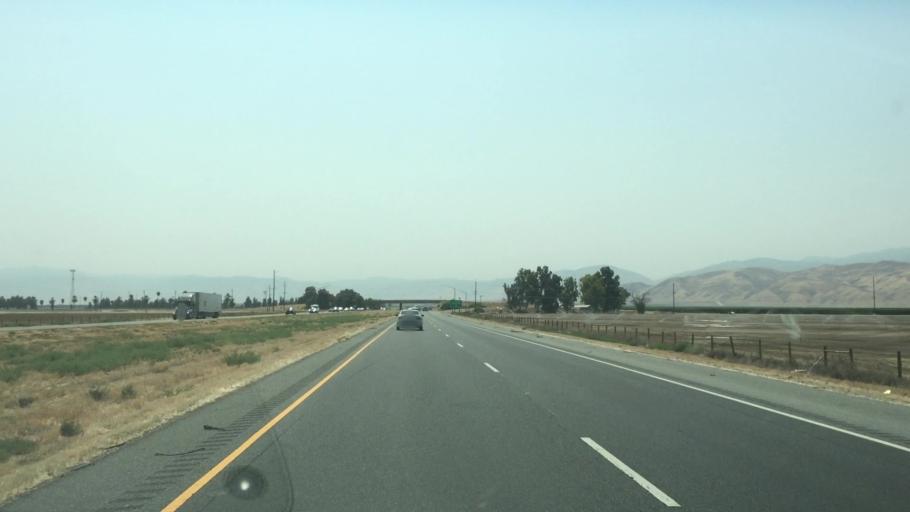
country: US
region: California
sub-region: Kern County
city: Greenfield
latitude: 35.0999
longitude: -119.0429
